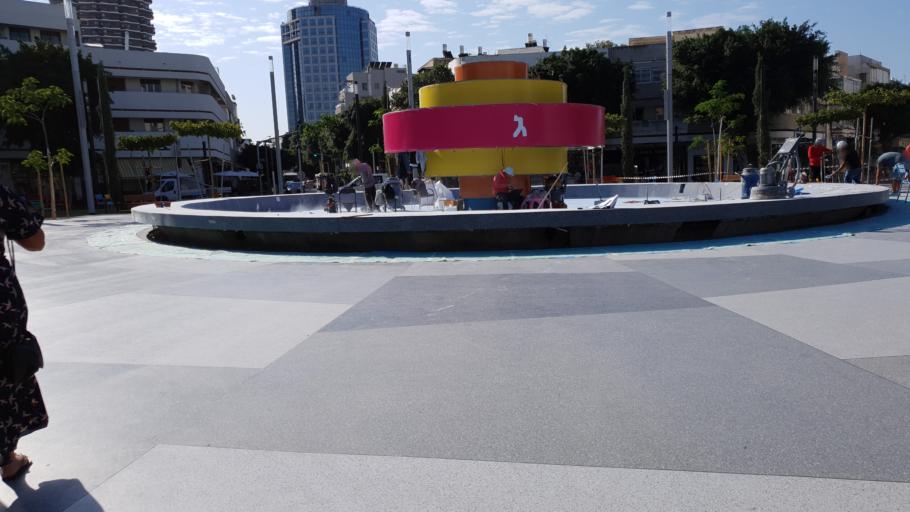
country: IL
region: Tel Aviv
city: Tel Aviv
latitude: 32.0781
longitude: 34.7742
